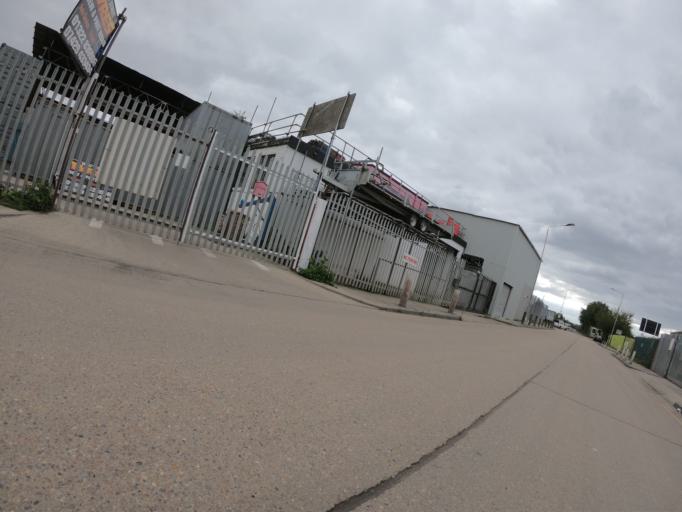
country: GB
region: England
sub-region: Essex
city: Purfleet
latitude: 51.4791
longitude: 0.2122
